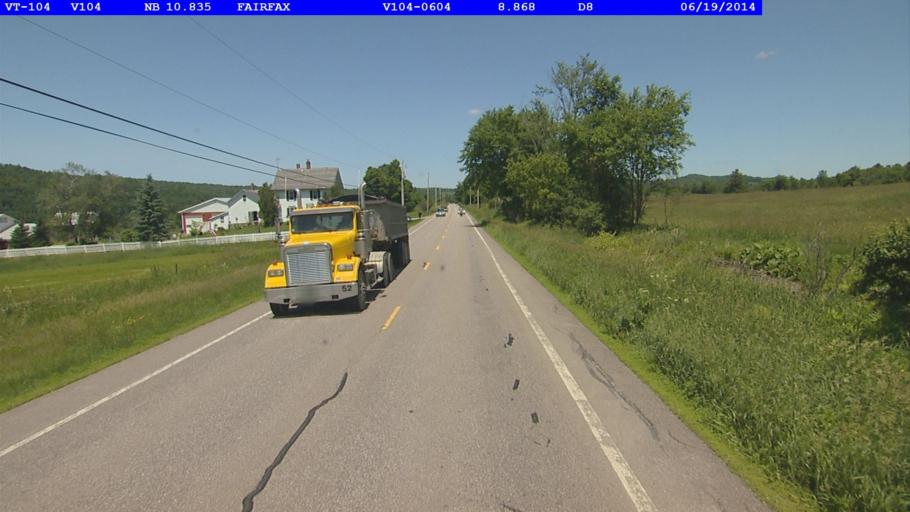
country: US
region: Vermont
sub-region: Chittenden County
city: Milton
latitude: 44.7122
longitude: -73.0389
